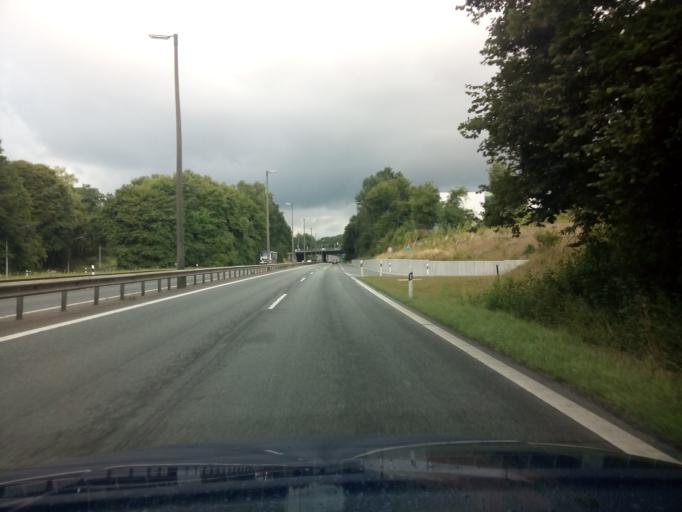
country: DE
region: Lower Saxony
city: Lemwerder
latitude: 53.1731
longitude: 8.6546
